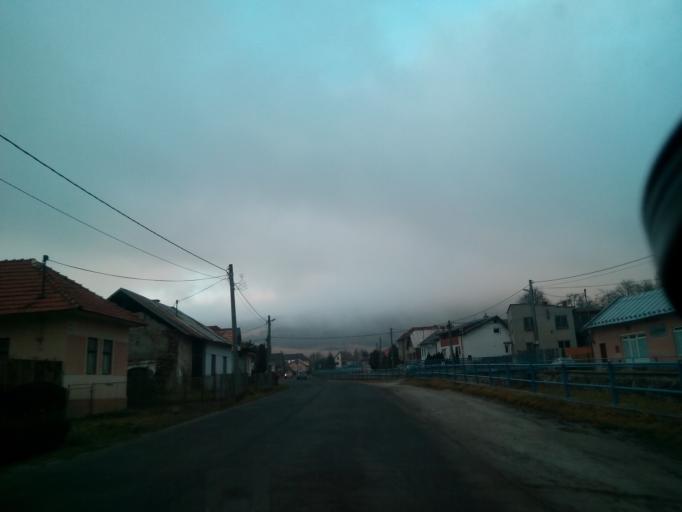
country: SK
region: Kosicky
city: Krompachy
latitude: 48.9288
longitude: 20.9407
